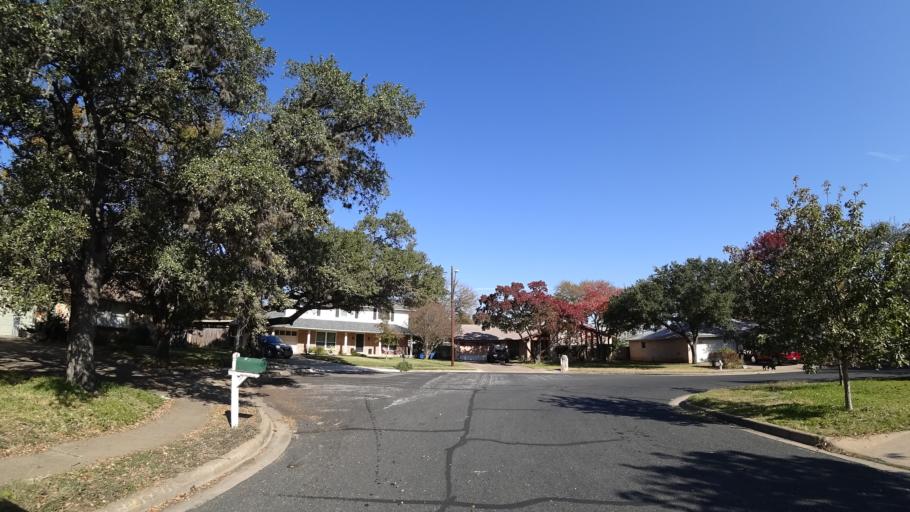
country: US
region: Texas
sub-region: Travis County
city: Barton Creek
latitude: 30.2329
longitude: -97.8478
